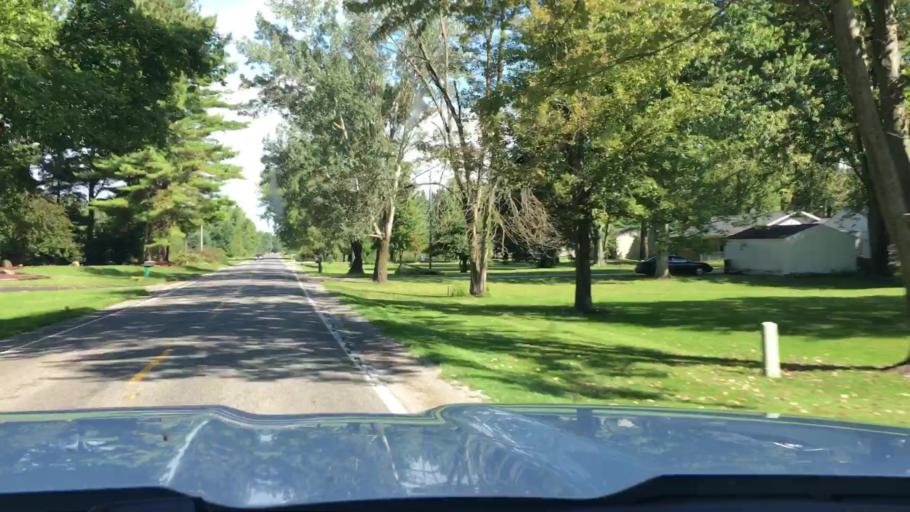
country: US
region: Michigan
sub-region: Saginaw County
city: Hemlock
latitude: 43.4728
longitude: -84.2303
